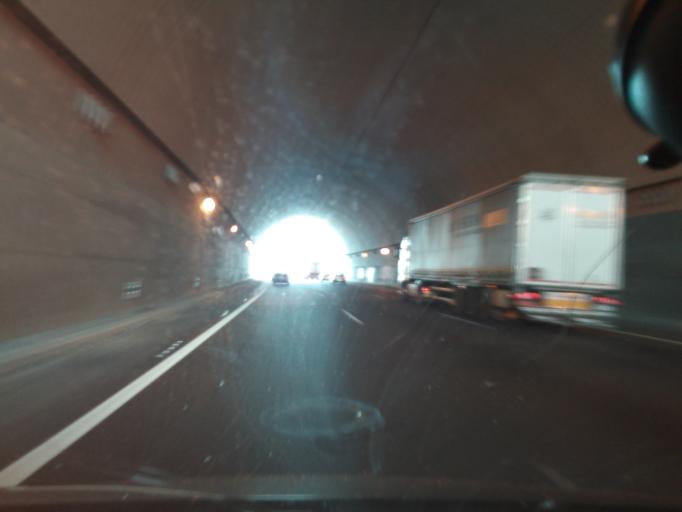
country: ES
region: Madrid
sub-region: Provincia de Madrid
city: San Fernando de Henares
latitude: 40.4050
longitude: -3.5267
